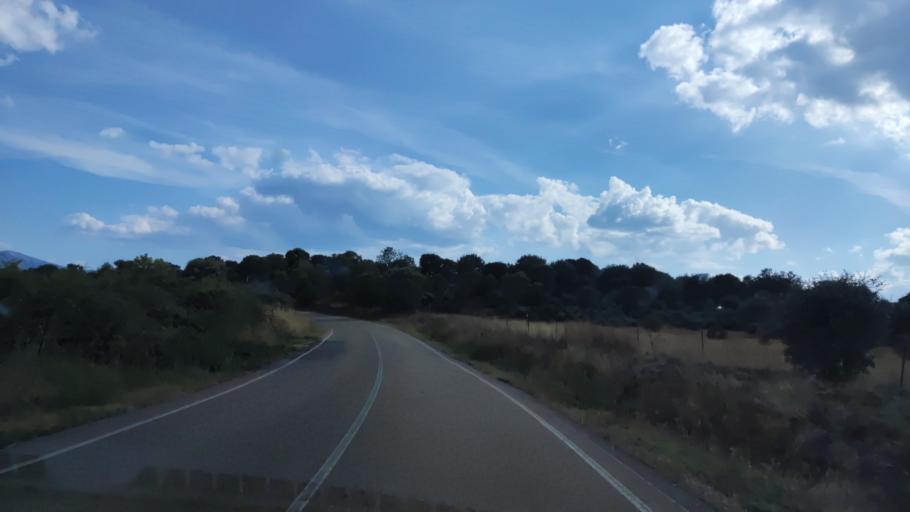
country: ES
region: Castille and Leon
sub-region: Provincia de Salamanca
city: Martiago
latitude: 40.4737
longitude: -6.4905
